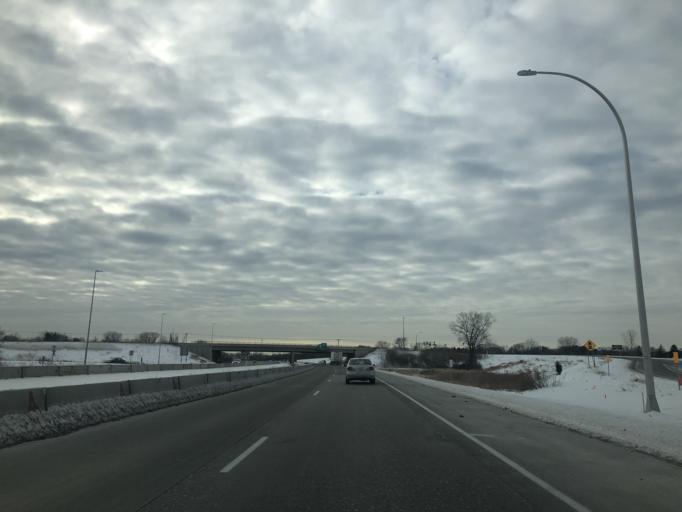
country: US
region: Minnesota
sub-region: Anoka County
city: Lexington
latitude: 45.1445
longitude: -93.1839
